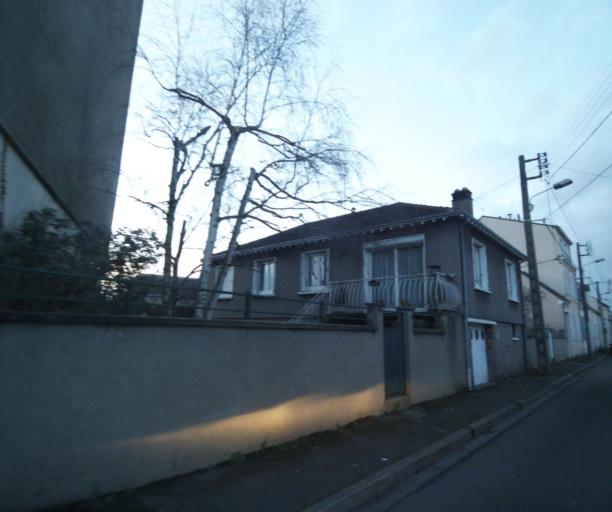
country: FR
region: Pays de la Loire
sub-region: Departement de la Sarthe
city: Le Mans
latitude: 47.9885
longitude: 0.2052
